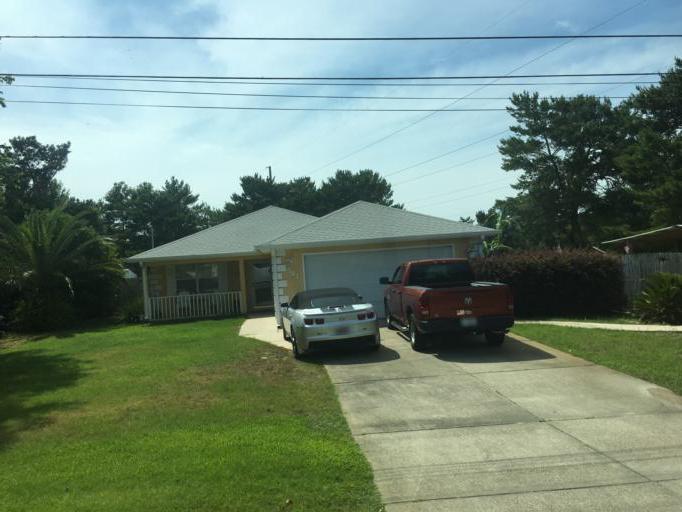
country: US
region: Florida
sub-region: Bay County
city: Laguna Beach
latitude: 30.2449
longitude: -85.9194
